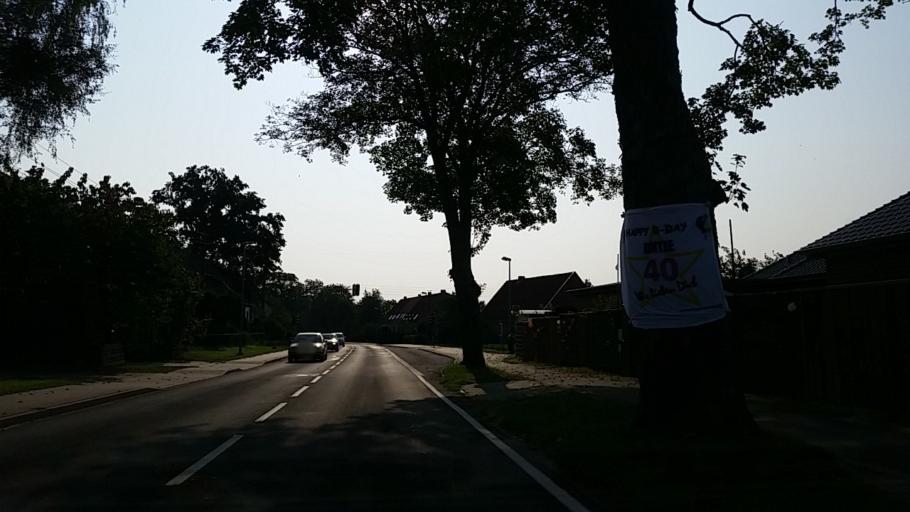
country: DE
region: Mecklenburg-Vorpommern
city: Hagenow
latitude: 53.4675
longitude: 11.1584
